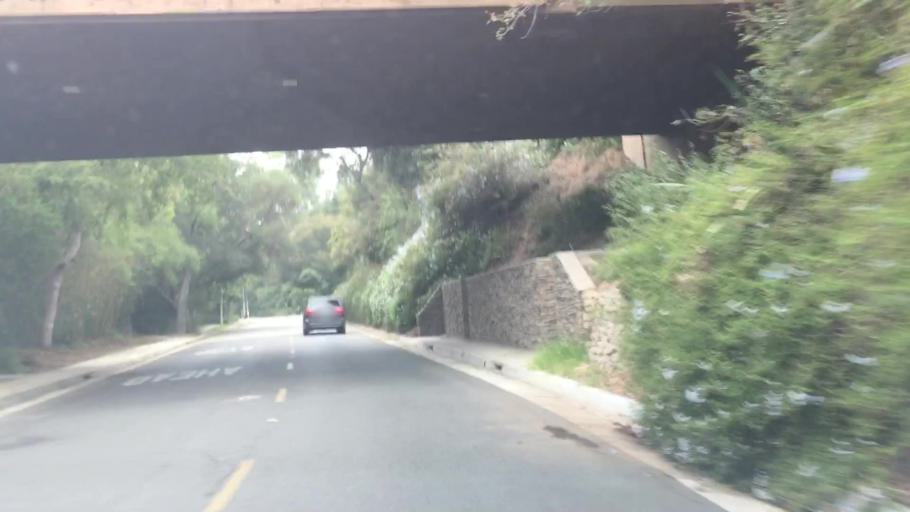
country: US
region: California
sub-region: Los Angeles County
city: San Marino
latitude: 34.1223
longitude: -118.1255
